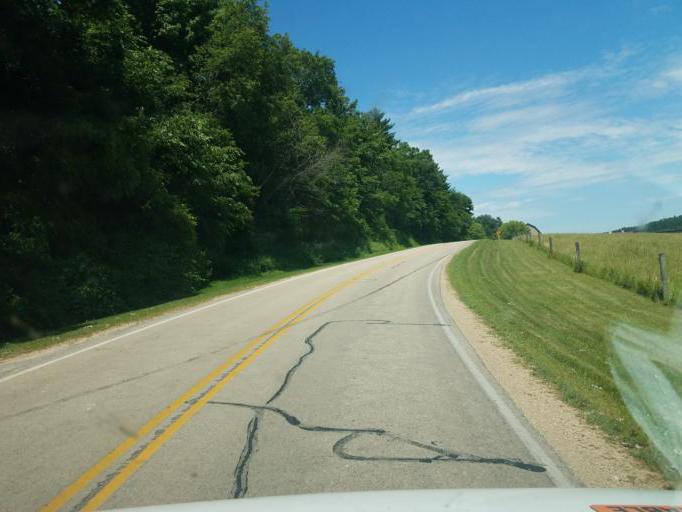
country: US
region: Wisconsin
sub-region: Vernon County
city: Hillsboro
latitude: 43.6303
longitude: -90.2313
